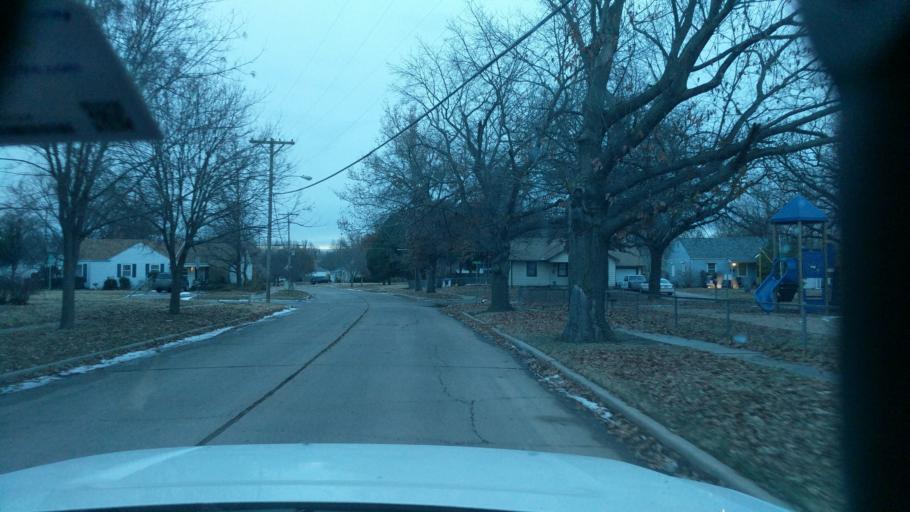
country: US
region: Kansas
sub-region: Sedgwick County
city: Wichita
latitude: 37.6675
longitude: -97.3083
